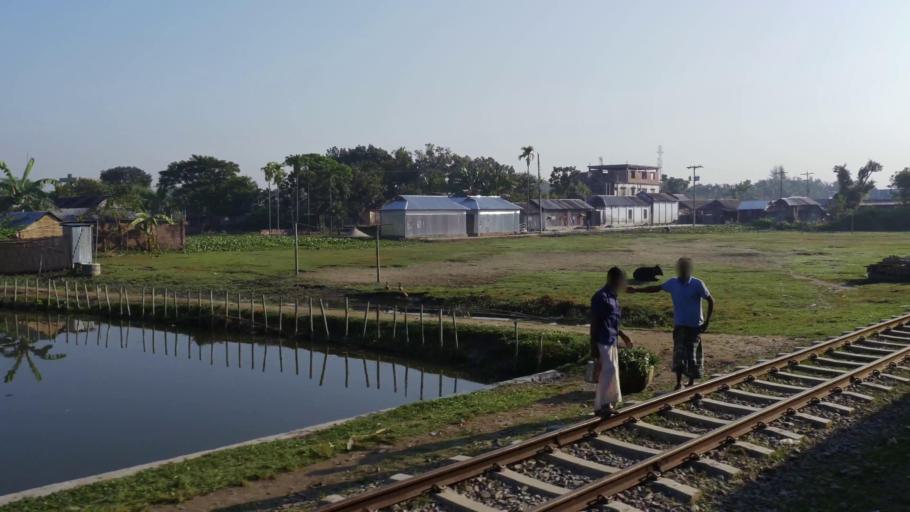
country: BD
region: Dhaka
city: Jamalpur
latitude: 24.8633
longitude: 90.1003
